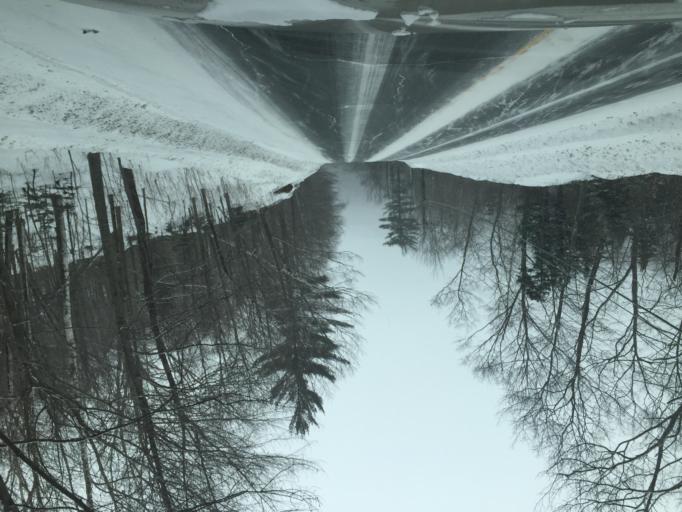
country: US
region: New Hampshire
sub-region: Carroll County
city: North Conway
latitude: 44.1965
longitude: -71.2324
